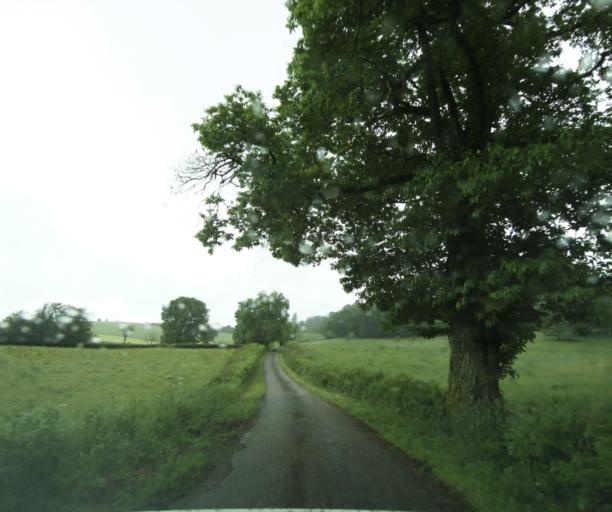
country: FR
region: Bourgogne
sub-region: Departement de Saone-et-Loire
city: Matour
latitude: 46.4196
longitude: 4.4754
